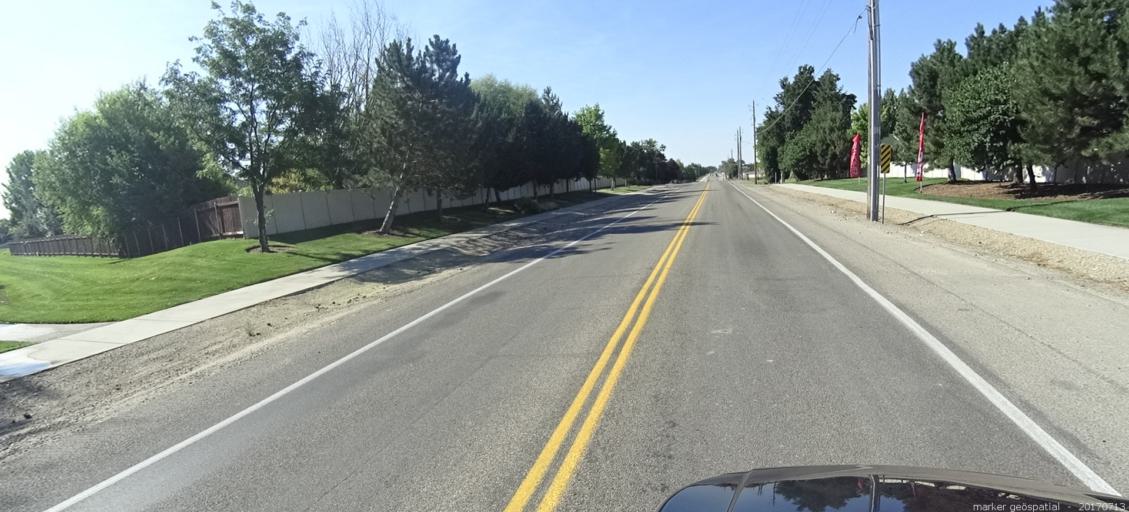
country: US
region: Idaho
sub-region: Ada County
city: Kuna
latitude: 43.5133
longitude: -116.4139
